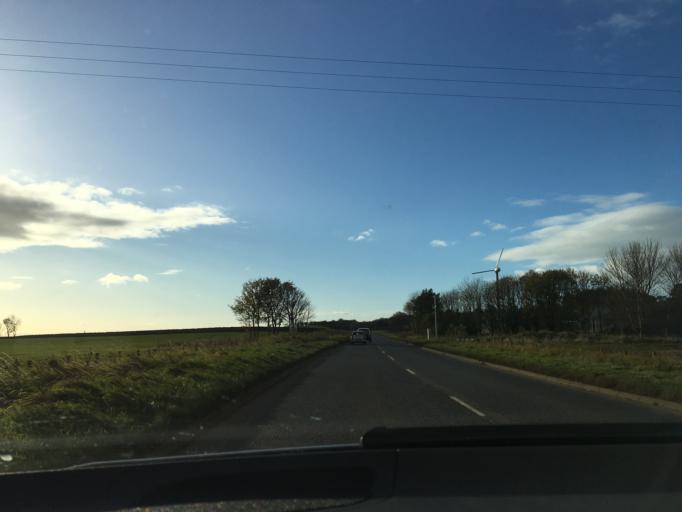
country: GB
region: Scotland
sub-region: East Lothian
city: North Berwick
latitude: 56.0454
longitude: -2.7738
